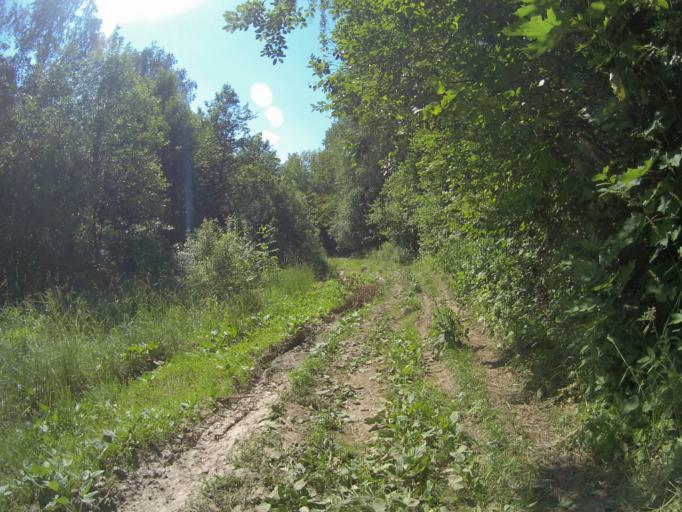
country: RU
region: Vladimir
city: Vorsha
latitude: 56.1698
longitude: 40.2065
